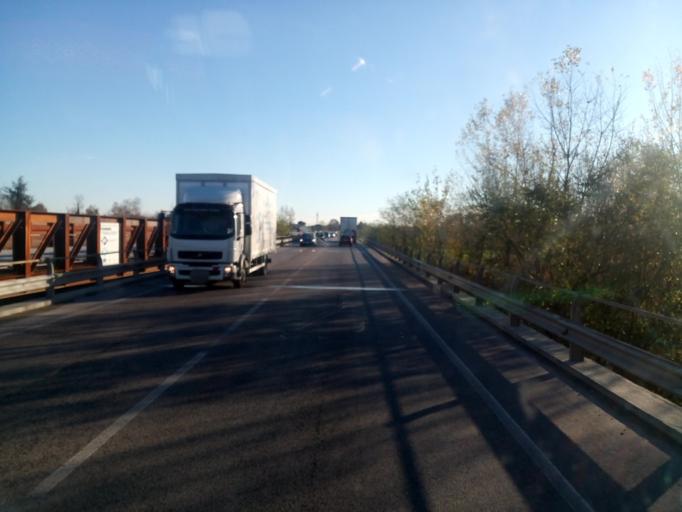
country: IT
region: Veneto
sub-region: Provincia di Vicenza
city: Cartigliano
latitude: 45.7382
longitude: 11.7000
